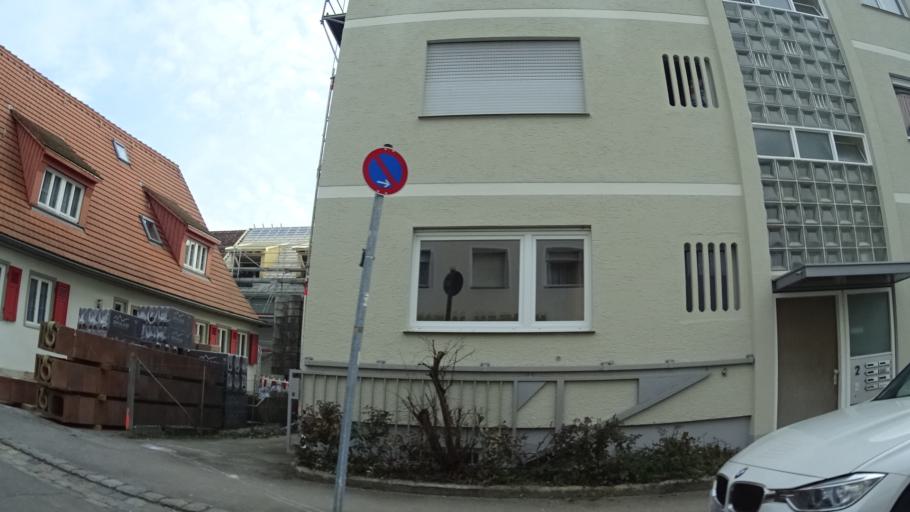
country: DE
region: Baden-Wuerttemberg
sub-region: Regierungsbezirk Stuttgart
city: Leinfelden-Echterdingen
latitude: 48.7267
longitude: 9.1451
